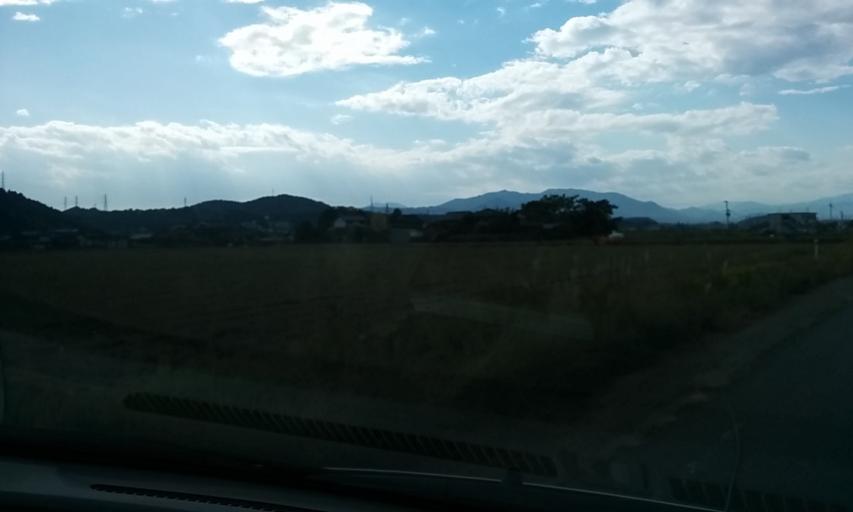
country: JP
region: Kyoto
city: Ayabe
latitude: 35.3063
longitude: 135.1864
